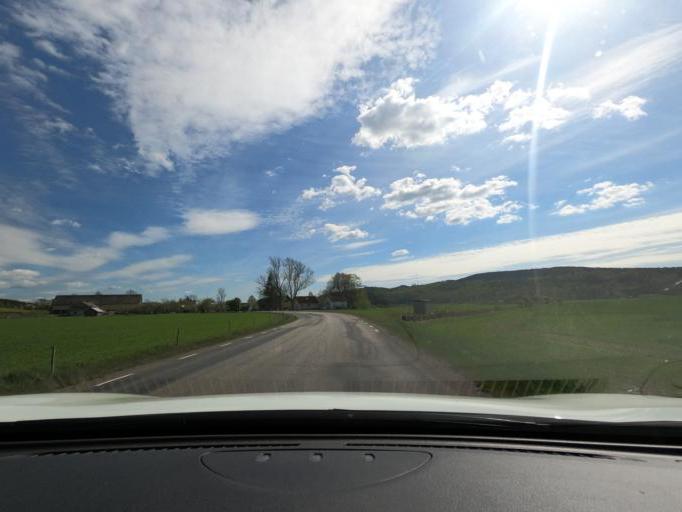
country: SE
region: Vaestra Goetaland
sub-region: Marks Kommun
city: Horred
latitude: 57.4453
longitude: 12.5112
